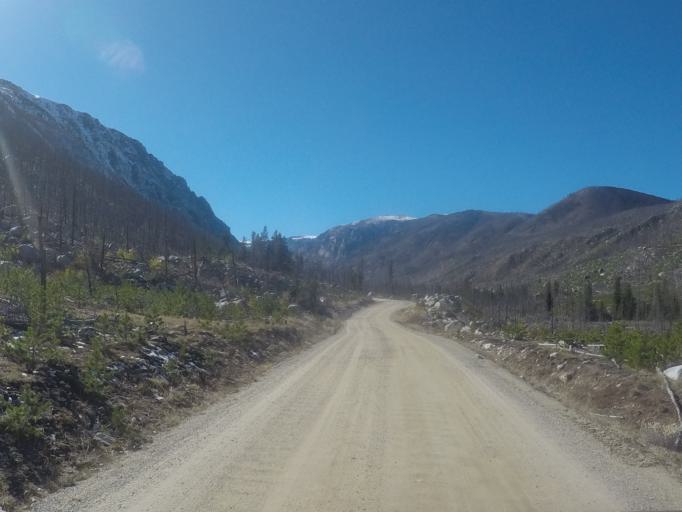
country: US
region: Montana
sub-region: Carbon County
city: Red Lodge
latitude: 45.1716
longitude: -109.4619
